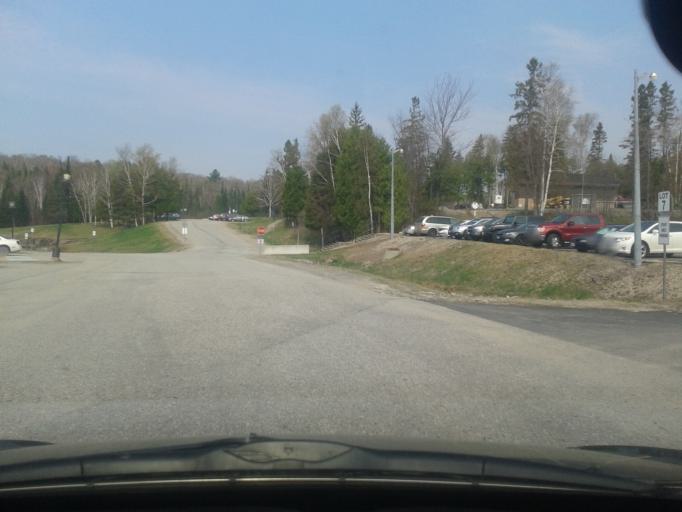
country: CA
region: Ontario
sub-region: Nipissing District
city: North Bay
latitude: 46.3453
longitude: -79.4918
